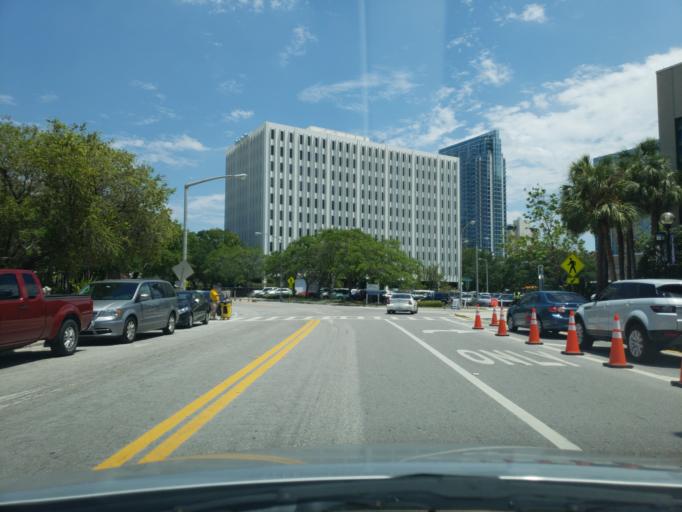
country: US
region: Florida
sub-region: Hillsborough County
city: Tampa
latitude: 27.9524
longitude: -82.4639
